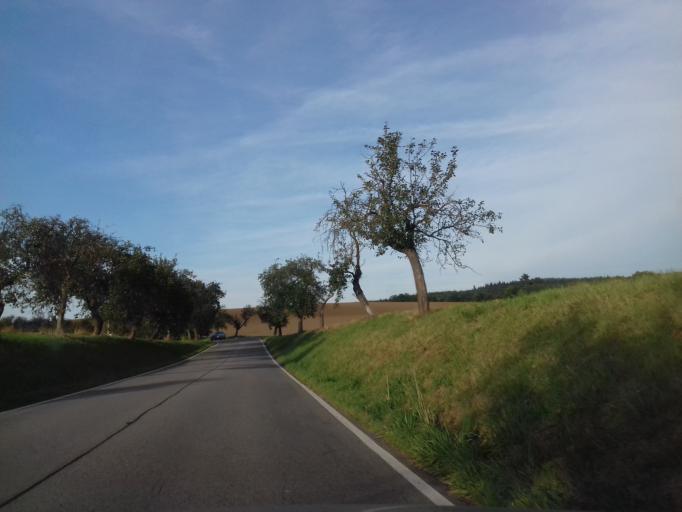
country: CZ
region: Central Bohemia
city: Kamenny Privoz
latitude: 49.8680
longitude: 14.5043
